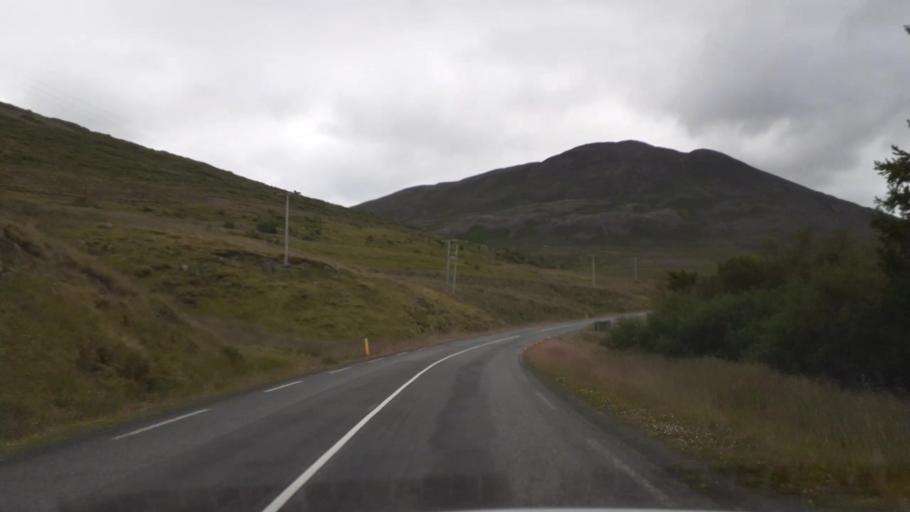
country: IS
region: Northeast
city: Akureyri
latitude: 65.8228
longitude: -18.0516
